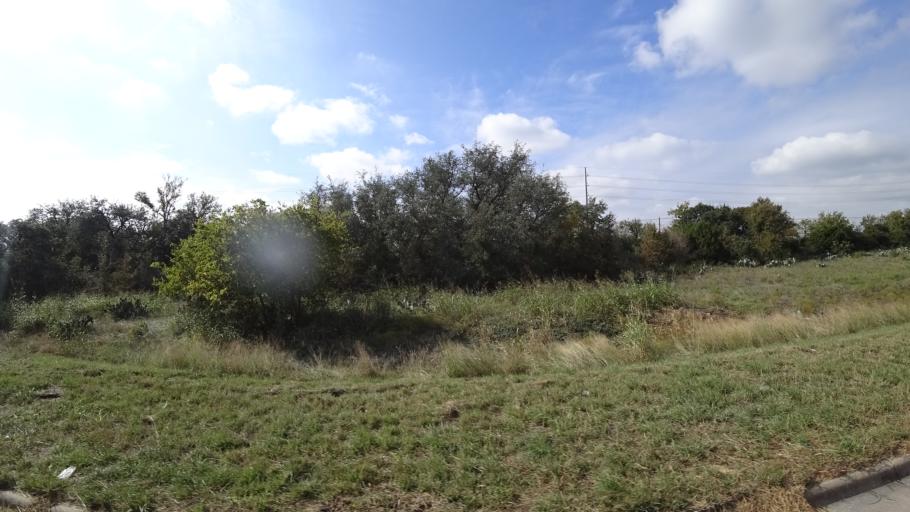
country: US
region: Texas
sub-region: Travis County
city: Wells Branch
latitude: 30.4478
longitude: -97.7155
